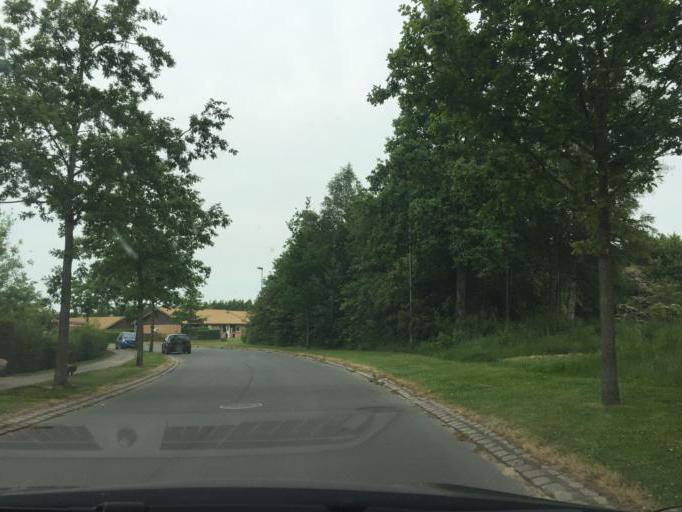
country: DK
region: South Denmark
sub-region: Odense Kommune
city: Neder Holluf
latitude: 55.3630
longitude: 10.4716
